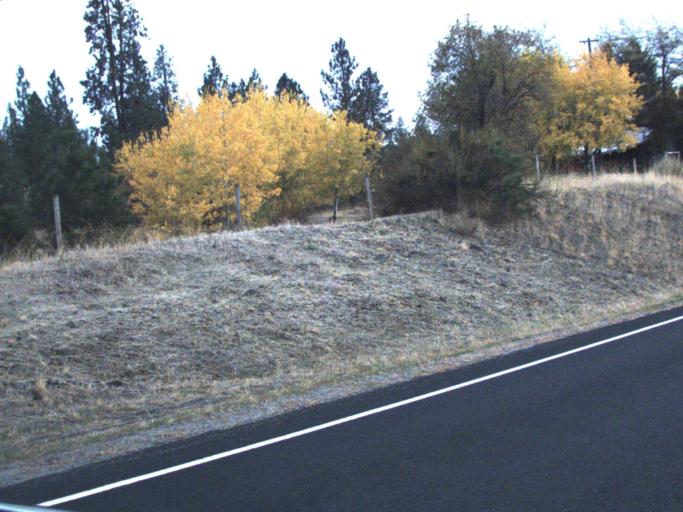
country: US
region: Washington
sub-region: Lincoln County
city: Davenport
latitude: 47.9364
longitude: -118.3182
